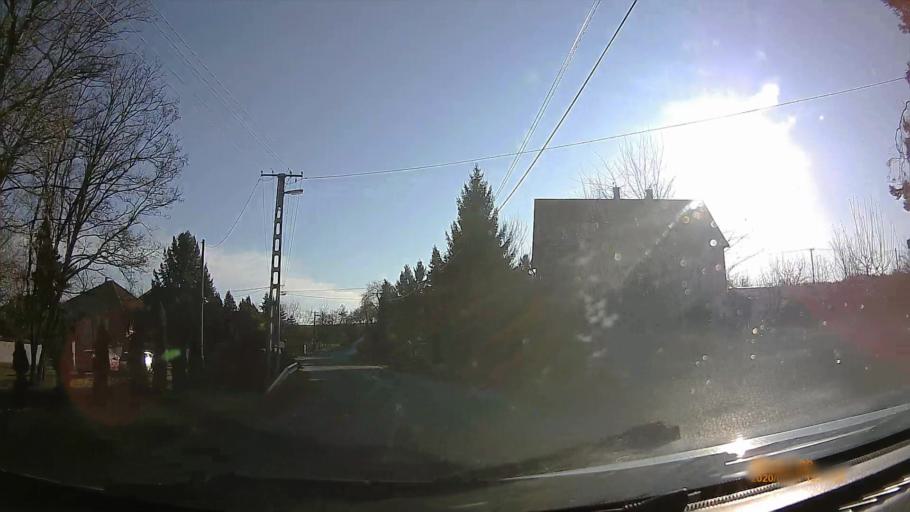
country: HU
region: Heves
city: Parad
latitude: 47.9356
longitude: 20.0243
